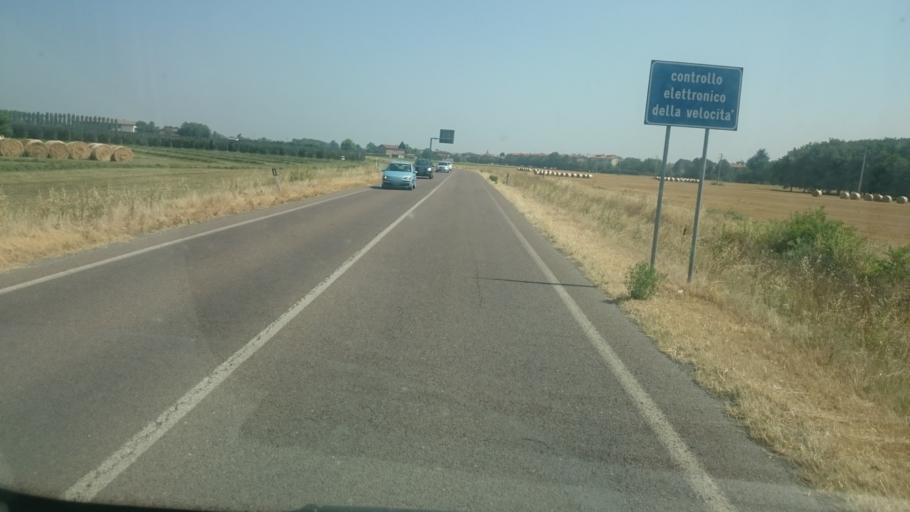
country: IT
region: Emilia-Romagna
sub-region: Provincia di Reggio Emilia
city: Fellegara
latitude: 44.6115
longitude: 10.7071
